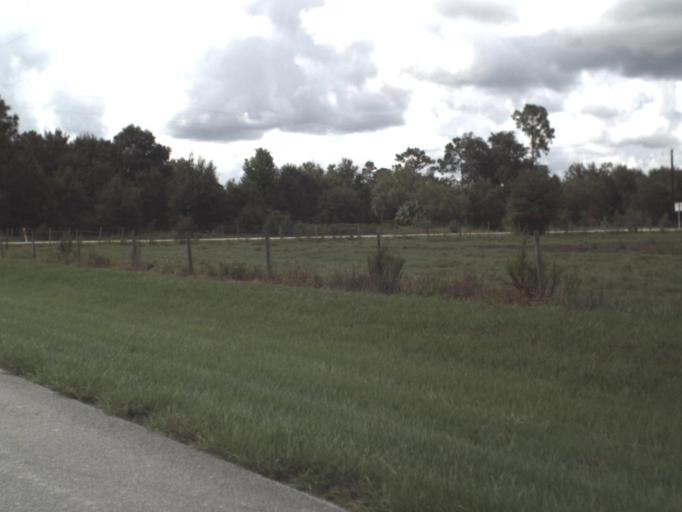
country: US
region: Florida
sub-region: DeSoto County
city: Nocatee
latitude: 27.2067
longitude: -82.0091
